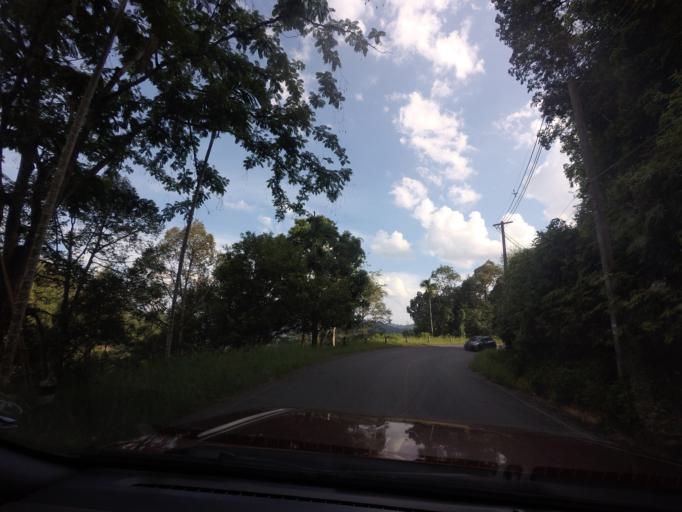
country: TH
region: Yala
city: Than To
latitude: 6.1424
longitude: 101.2901
